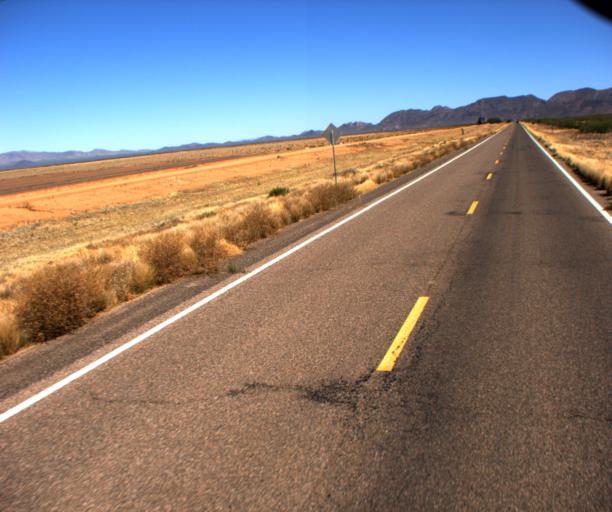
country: US
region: Arizona
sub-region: Yavapai County
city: Congress
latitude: 33.9559
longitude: -113.1416
